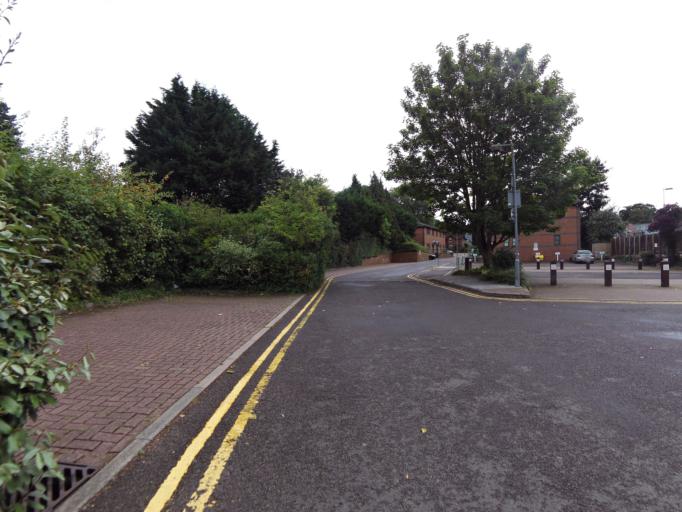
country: GB
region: England
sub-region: Hertfordshire
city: Radlett
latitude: 51.6861
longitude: -0.3172
